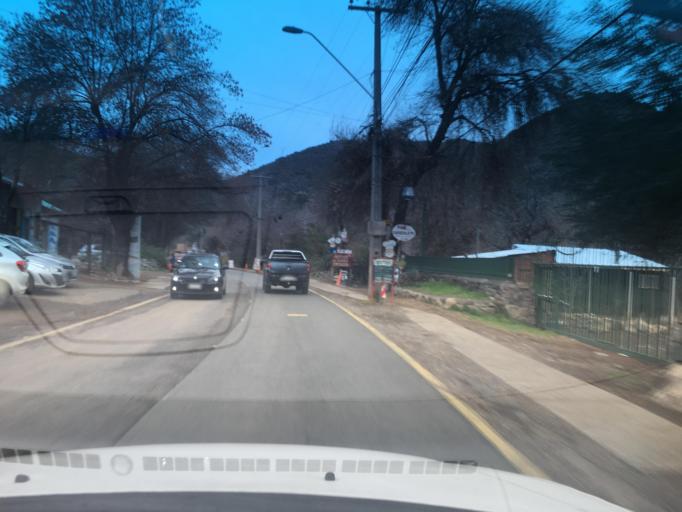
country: CL
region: Santiago Metropolitan
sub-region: Provincia de Cordillera
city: Puente Alto
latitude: -33.7320
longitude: -70.3133
